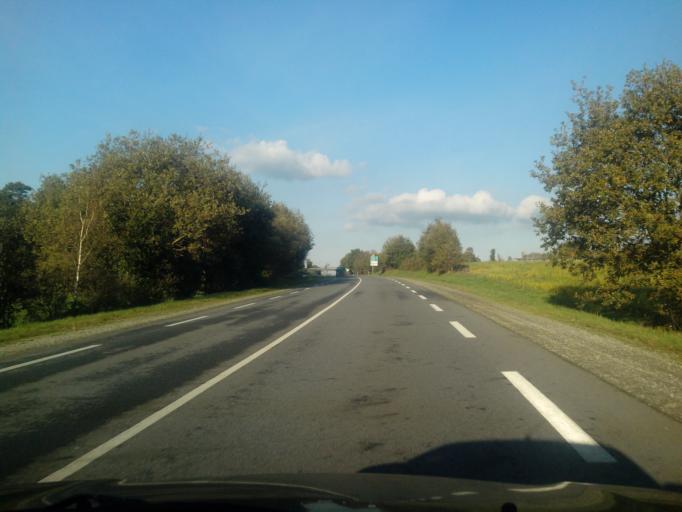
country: FR
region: Brittany
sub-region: Departement du Morbihan
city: Loyat
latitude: 47.9797
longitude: -2.3743
